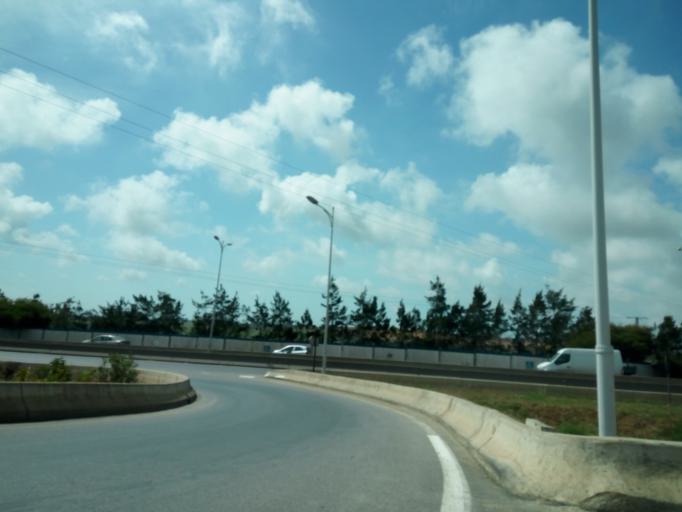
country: DZ
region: Tipaza
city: Douera
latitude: 36.6986
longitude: 2.9669
